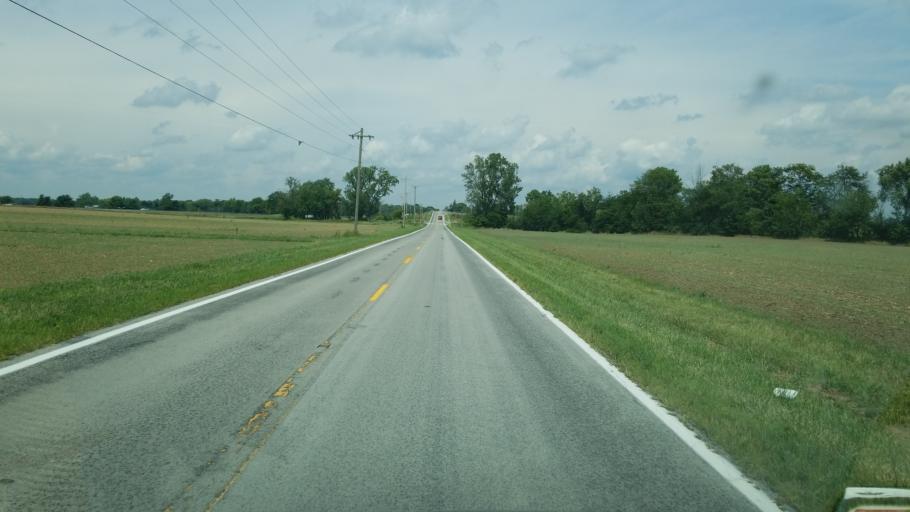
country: US
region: Ohio
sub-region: Hancock County
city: Findlay
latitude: 40.9721
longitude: -83.7274
